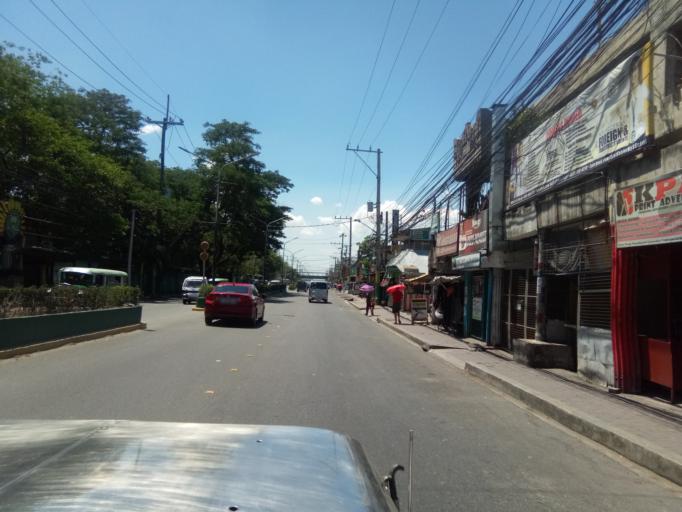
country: PH
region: Calabarzon
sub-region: Province of Cavite
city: Dasmarinas
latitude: 14.3254
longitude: 120.9618
